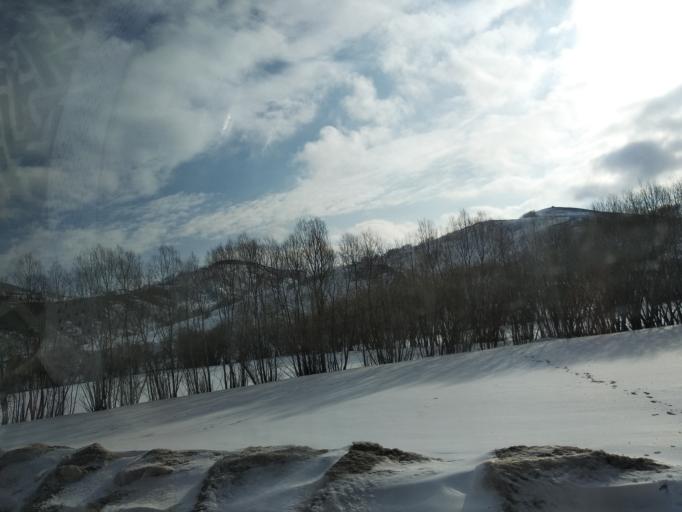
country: TR
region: Erzincan
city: Catalarmut
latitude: 39.9090
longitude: 39.4059
